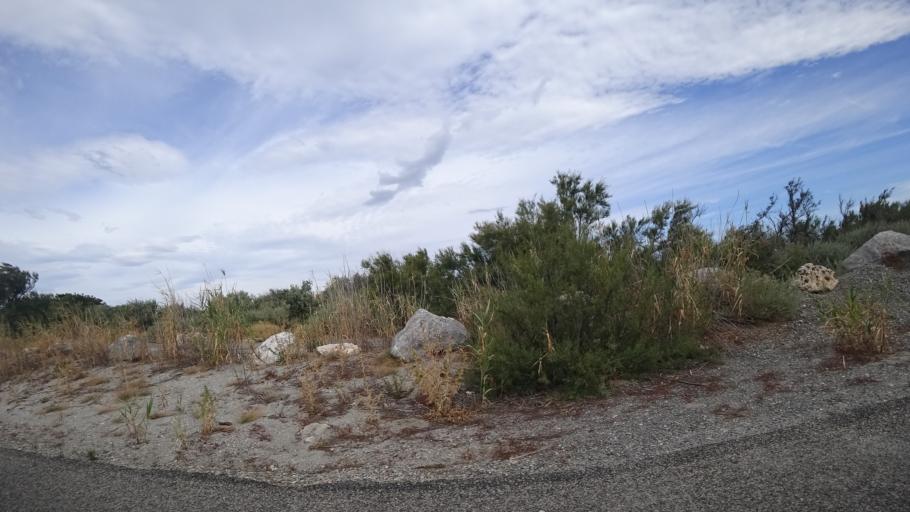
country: FR
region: Languedoc-Roussillon
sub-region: Departement de l'Aude
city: Leucate
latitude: 42.8681
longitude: 3.0331
